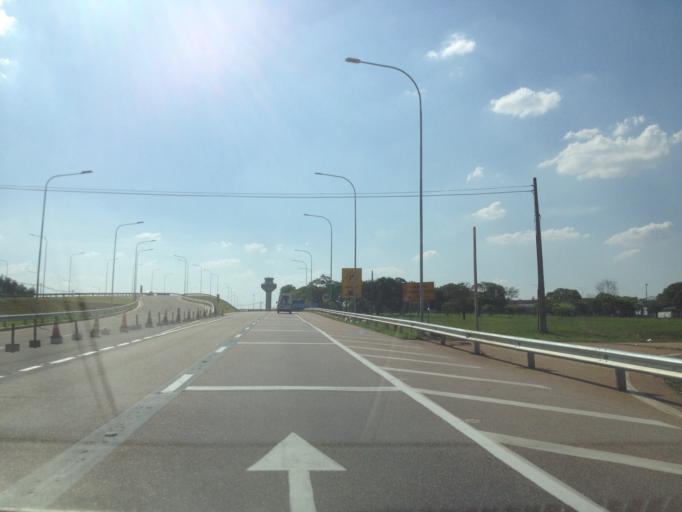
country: BR
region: Sao Paulo
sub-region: Indaiatuba
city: Indaiatuba
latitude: -23.0159
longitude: -47.1382
